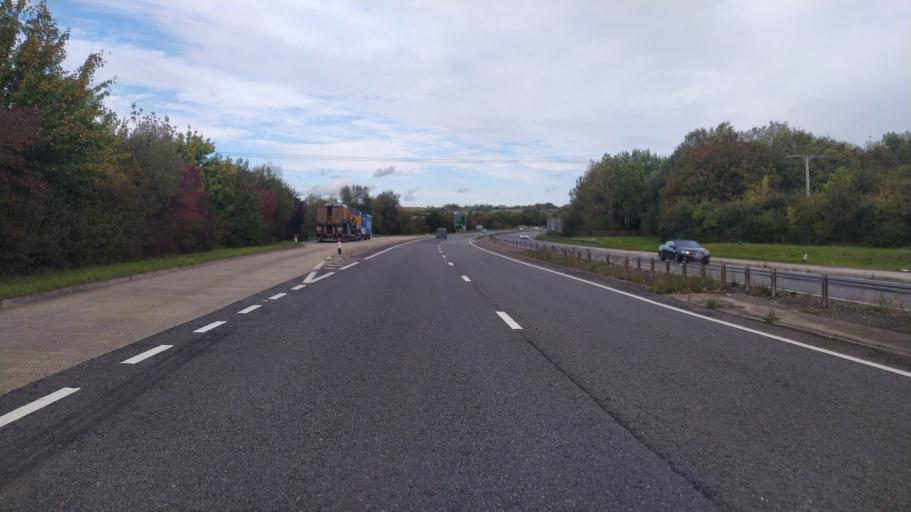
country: GB
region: England
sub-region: Dorset
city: Dorchester
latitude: 50.7501
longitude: -2.3560
